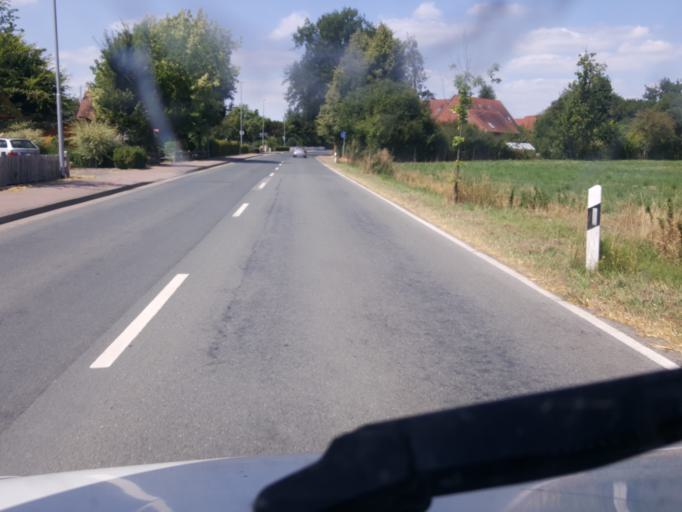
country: DE
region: North Rhine-Westphalia
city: Bad Oeynhausen
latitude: 52.2402
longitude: 8.7503
